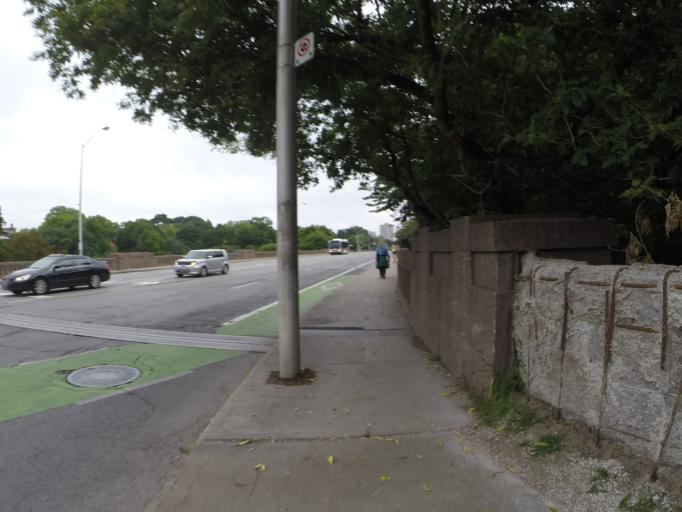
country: CA
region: Ontario
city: Toronto
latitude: 43.6706
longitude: -79.3704
